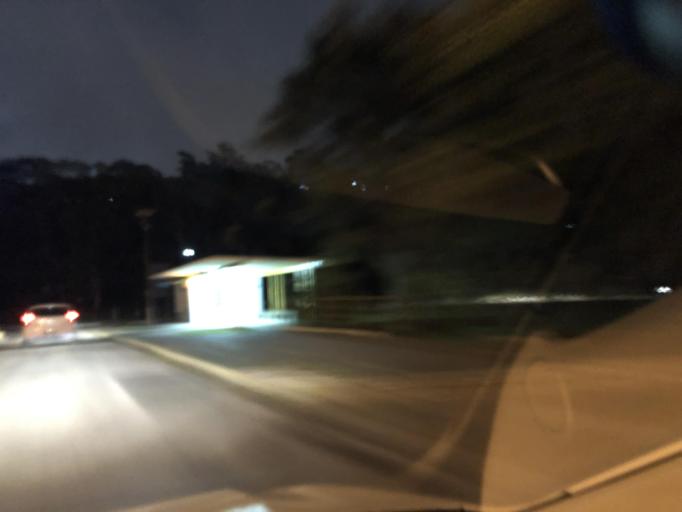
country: BR
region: Santa Catarina
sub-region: Florianopolis
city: Carvoeira
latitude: -27.6016
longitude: -48.5245
